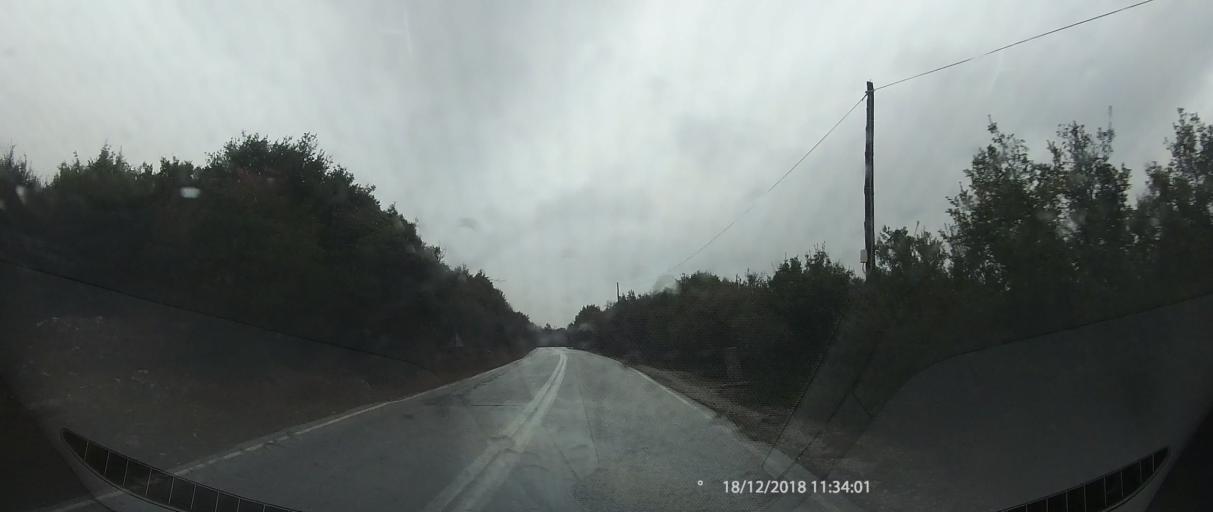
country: GR
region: Central Macedonia
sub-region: Nomos Pierias
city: Litochoro
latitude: 40.1133
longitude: 22.4910
